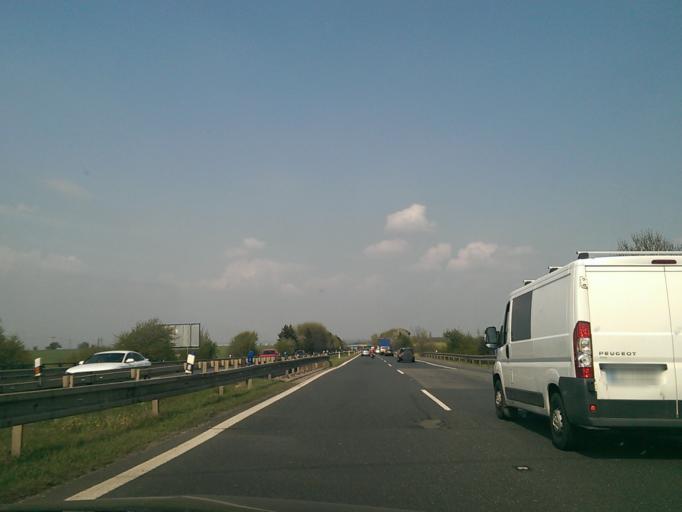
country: CZ
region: Central Bohemia
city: Zelenec
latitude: 50.1520
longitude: 14.6581
